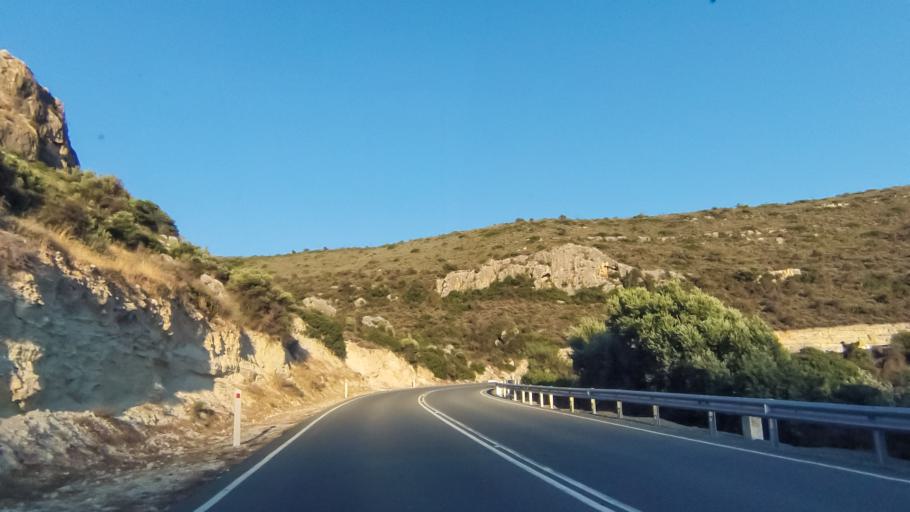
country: CY
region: Limassol
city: Sotira
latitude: 34.6755
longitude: 32.8235
